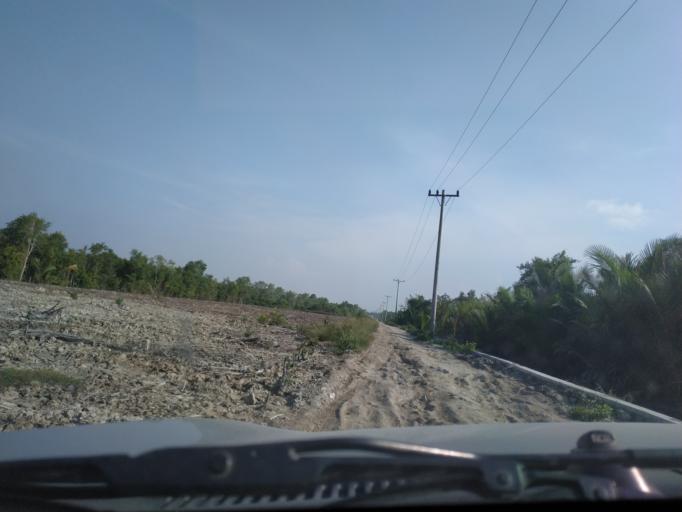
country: ID
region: North Sumatra
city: Teluk Nibung
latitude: 3.1033
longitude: 99.7773
